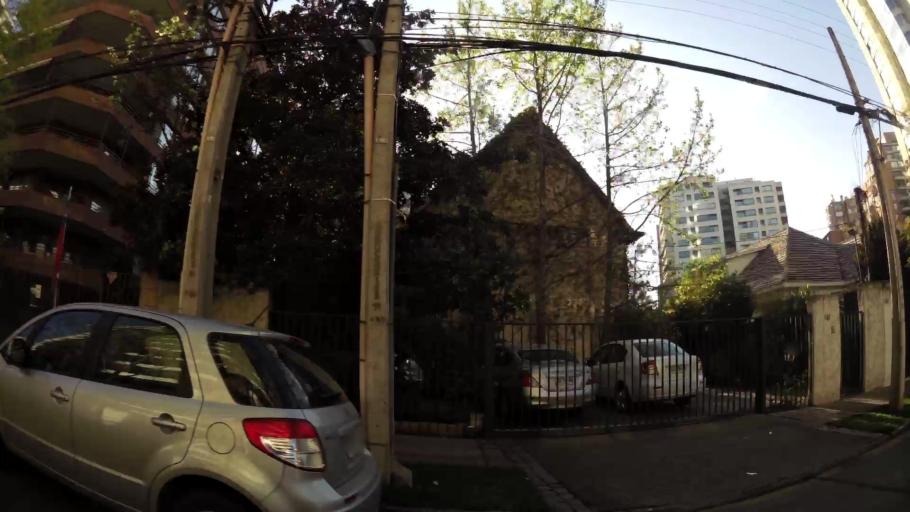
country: CL
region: Santiago Metropolitan
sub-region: Provincia de Santiago
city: Villa Presidente Frei, Nunoa, Santiago, Chile
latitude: -33.4137
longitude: -70.5908
